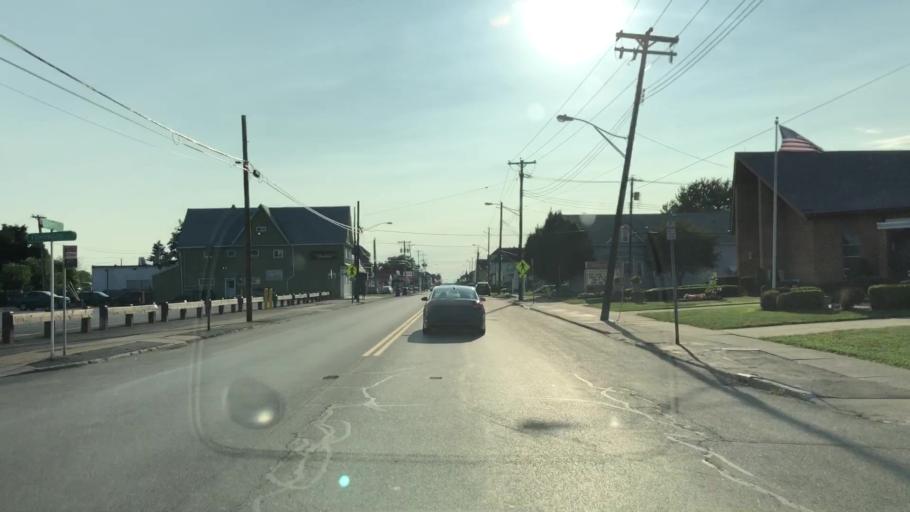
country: US
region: New York
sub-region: Erie County
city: Sloan
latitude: 42.8717
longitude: -78.7961
